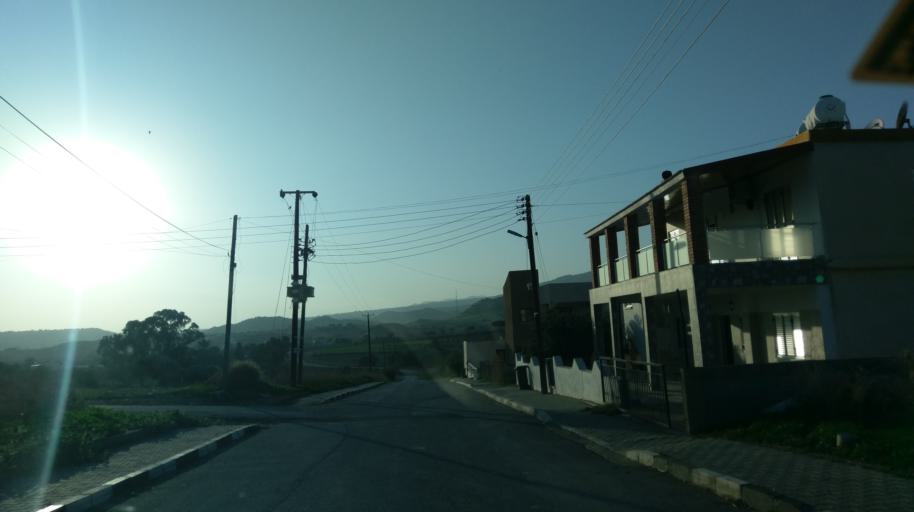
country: CY
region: Ammochostos
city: Trikomo
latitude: 35.3659
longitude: 33.9361
